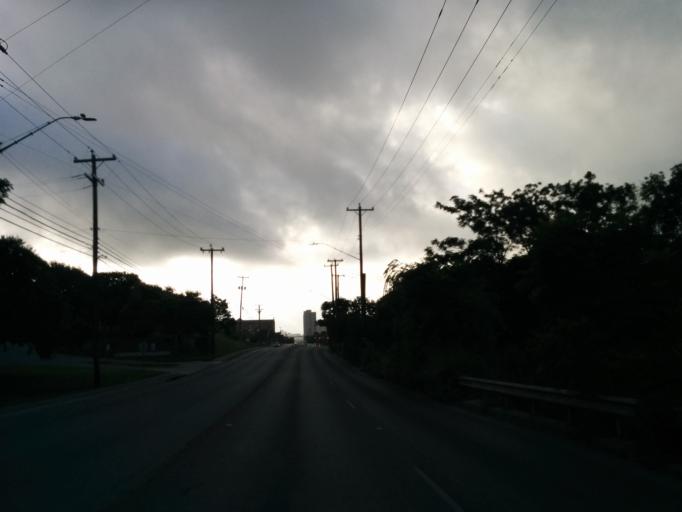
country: US
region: Texas
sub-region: Bexar County
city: Olmos Park
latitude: 29.4655
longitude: -98.4771
